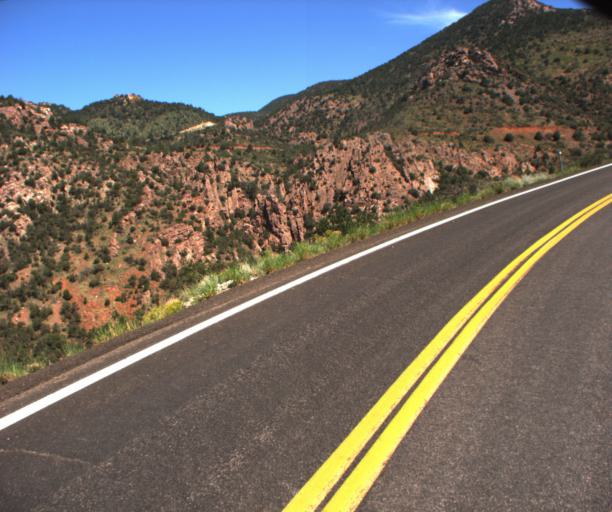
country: US
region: Arizona
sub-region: Greenlee County
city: Morenci
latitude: 33.1663
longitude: -109.3662
